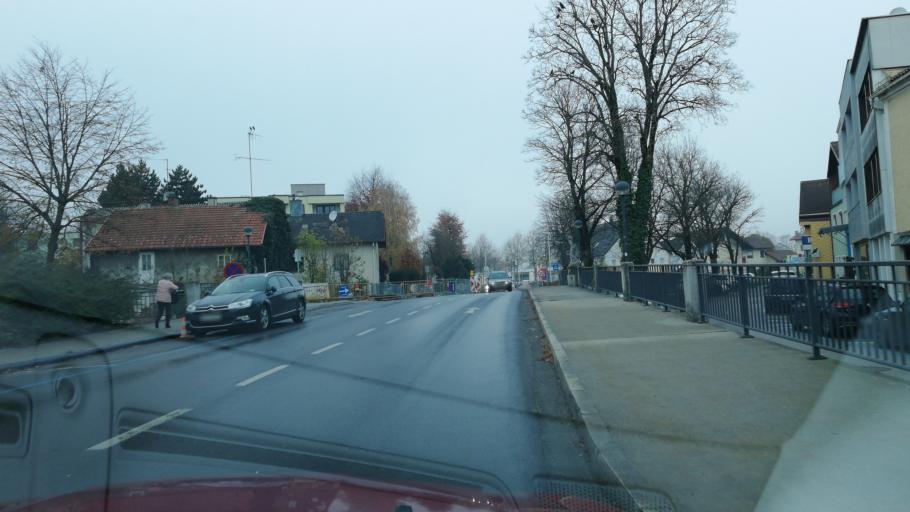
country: AT
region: Upper Austria
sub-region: Politischer Bezirk Ried im Innkreis
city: Ried im Innkreis
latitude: 48.2114
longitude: 13.4876
